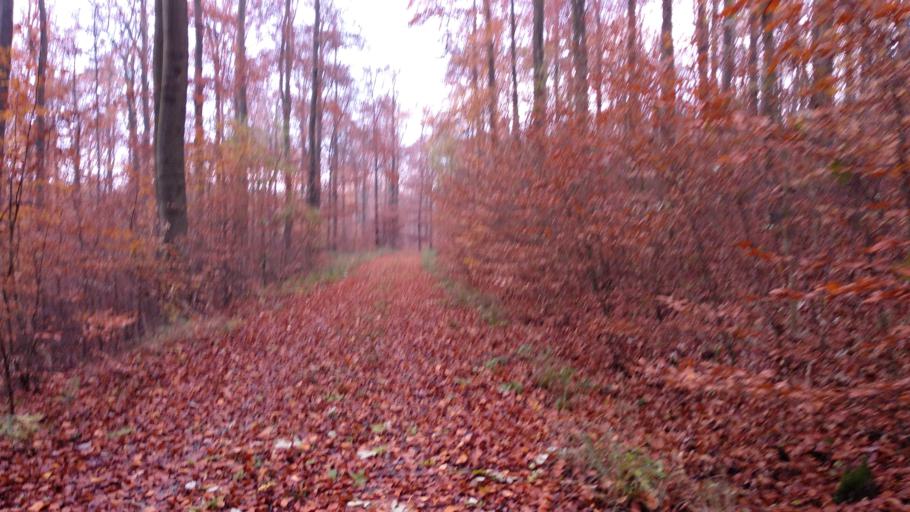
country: DE
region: North Rhine-Westphalia
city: Beverungen
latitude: 51.6621
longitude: 9.3217
